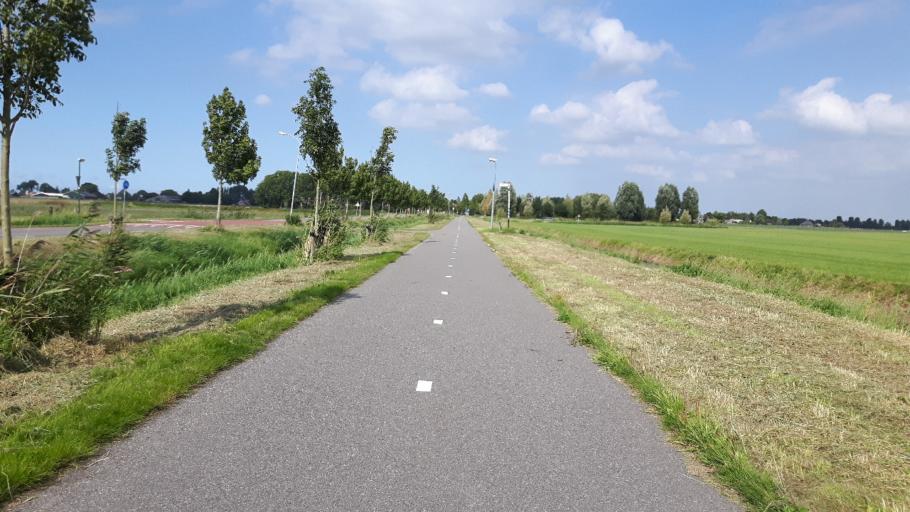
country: NL
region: North Holland
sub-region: Gemeente Medemblik
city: Opperdoes
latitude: 52.7174
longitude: 5.0917
